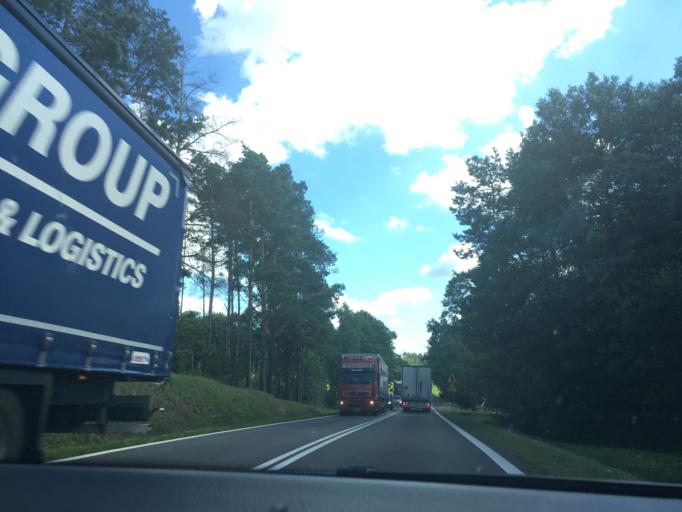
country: PL
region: Podlasie
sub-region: Powiat sokolski
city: Suchowola
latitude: 53.6614
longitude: 23.1264
